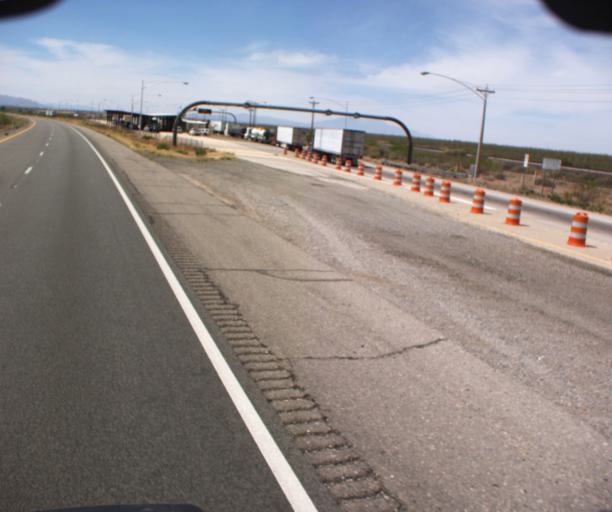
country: US
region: New Mexico
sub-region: Hidalgo County
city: Lordsburg
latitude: 32.2572
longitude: -109.1774
